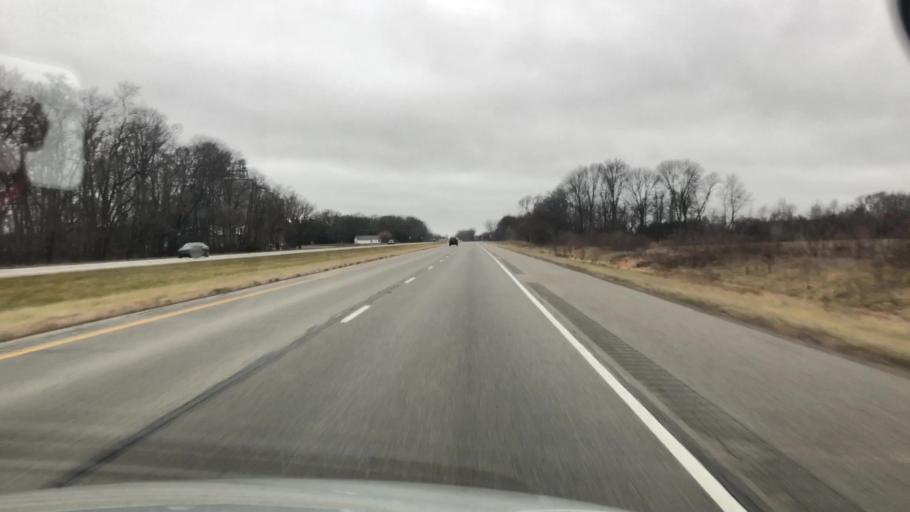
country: US
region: Indiana
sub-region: Kosciusko County
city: Mentone
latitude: 41.2697
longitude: -86.0057
